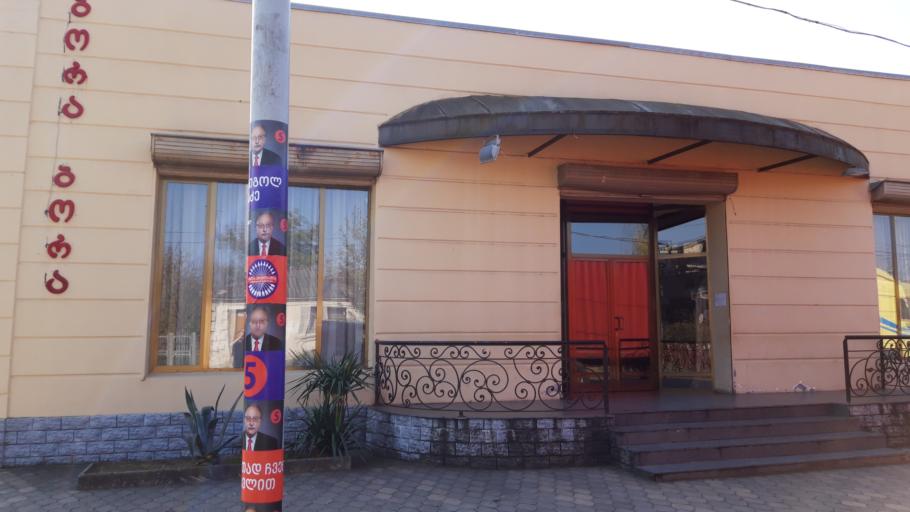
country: GE
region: Imereti
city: Samtredia
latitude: 42.1621
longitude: 42.3393
